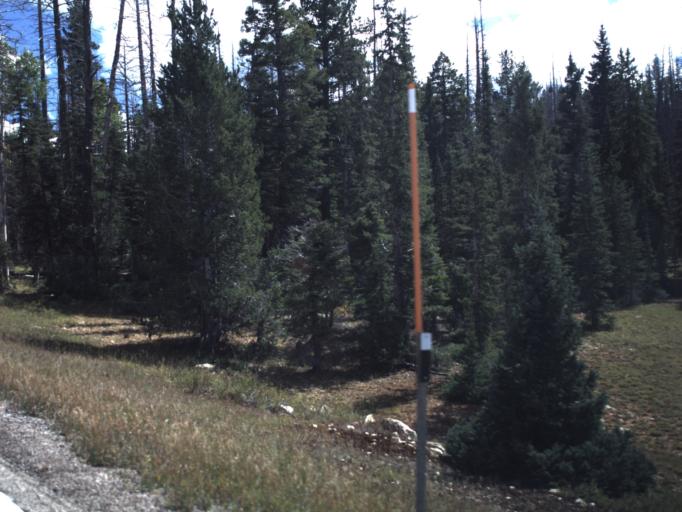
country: US
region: Utah
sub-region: Iron County
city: Parowan
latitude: 37.5319
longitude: -112.7674
